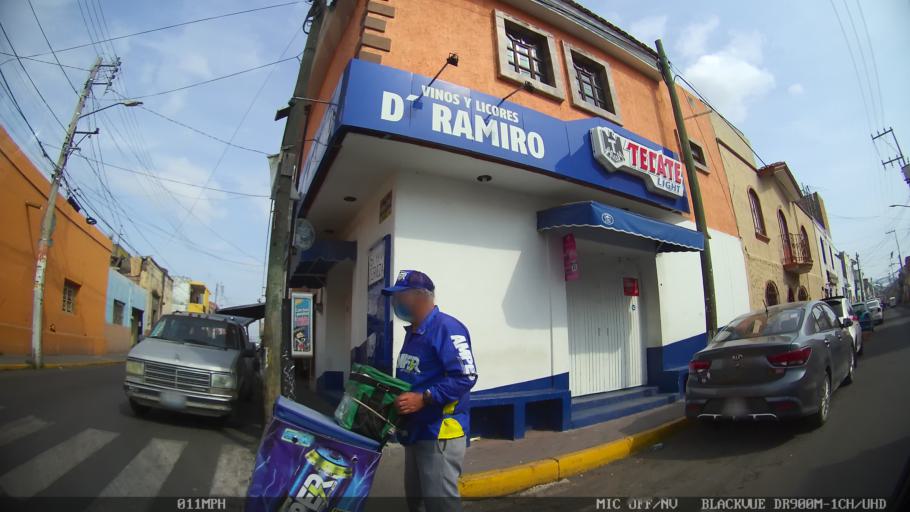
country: MX
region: Jalisco
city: Tonala
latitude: 20.6223
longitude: -103.2407
